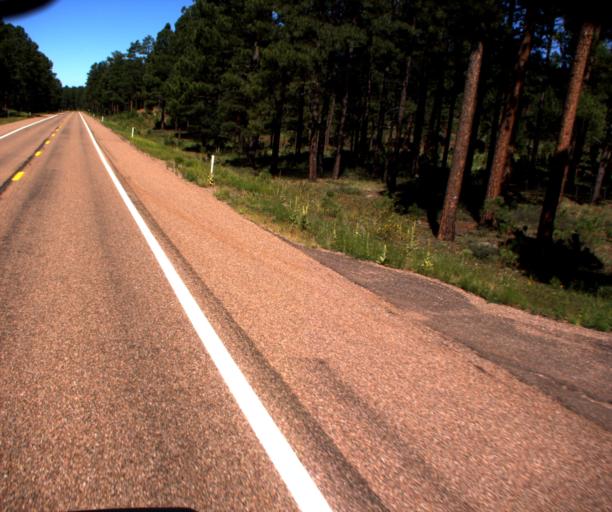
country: US
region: Arizona
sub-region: Navajo County
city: Pinetop-Lakeside
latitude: 34.0796
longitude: -109.8108
